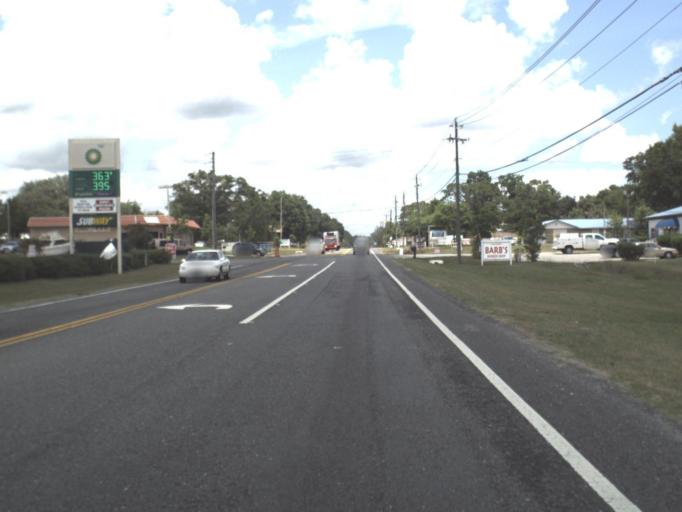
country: US
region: Florida
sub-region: Nassau County
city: Yulee
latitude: 30.6005
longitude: -81.5986
